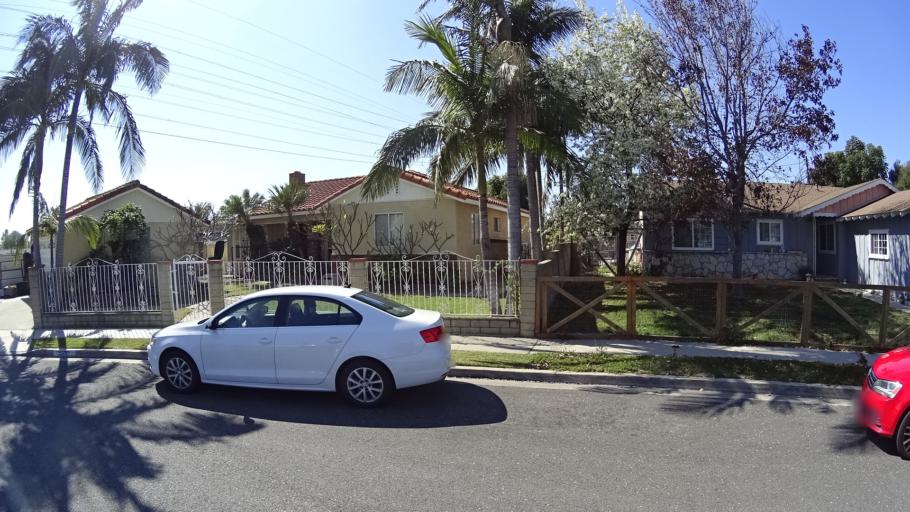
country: US
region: California
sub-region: Orange County
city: Garden Grove
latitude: 33.8076
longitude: -117.9443
